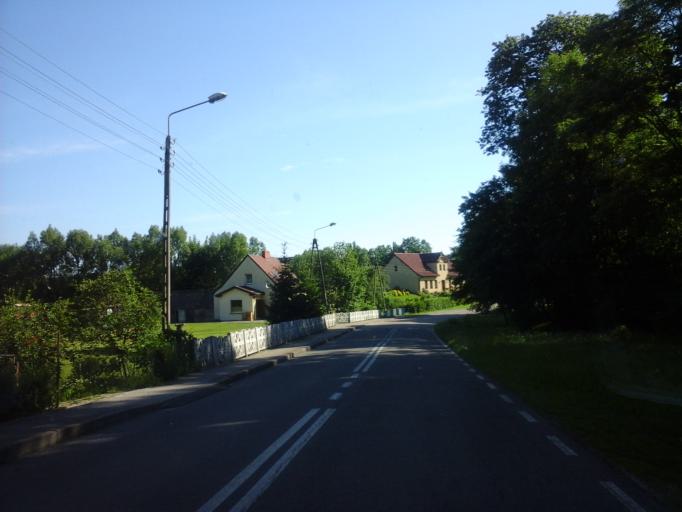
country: PL
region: West Pomeranian Voivodeship
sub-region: Powiat drawski
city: Zlocieniec
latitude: 53.6277
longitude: 15.9300
